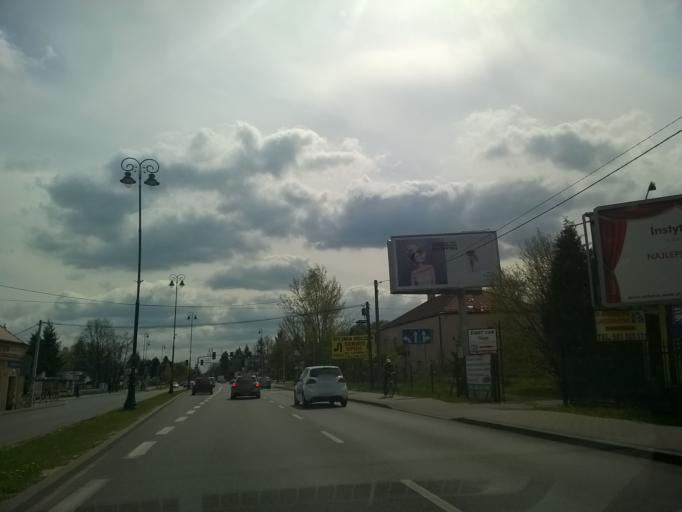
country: PL
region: Masovian Voivodeship
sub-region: Powiat piaseczynski
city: Konstancin-Jeziorna
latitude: 52.1030
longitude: 21.1142
